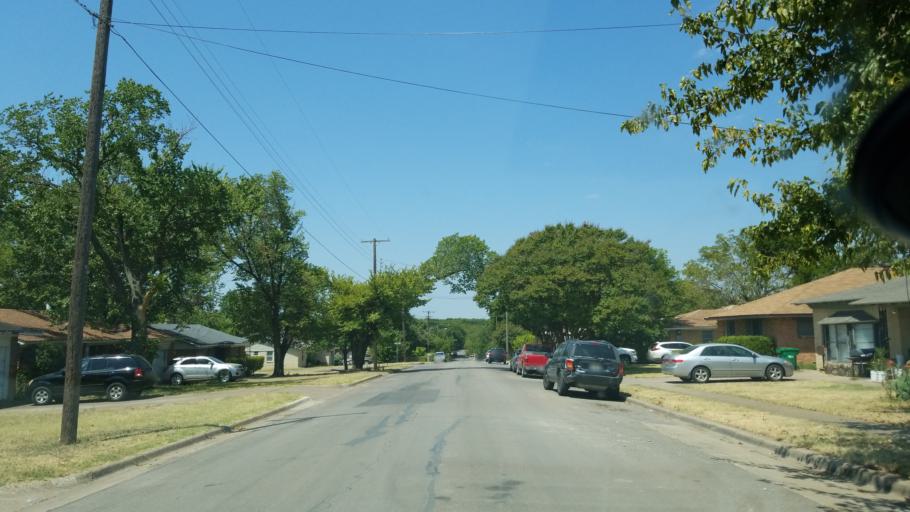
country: US
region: Texas
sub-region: Dallas County
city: Cockrell Hill
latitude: 32.7342
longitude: -96.8934
